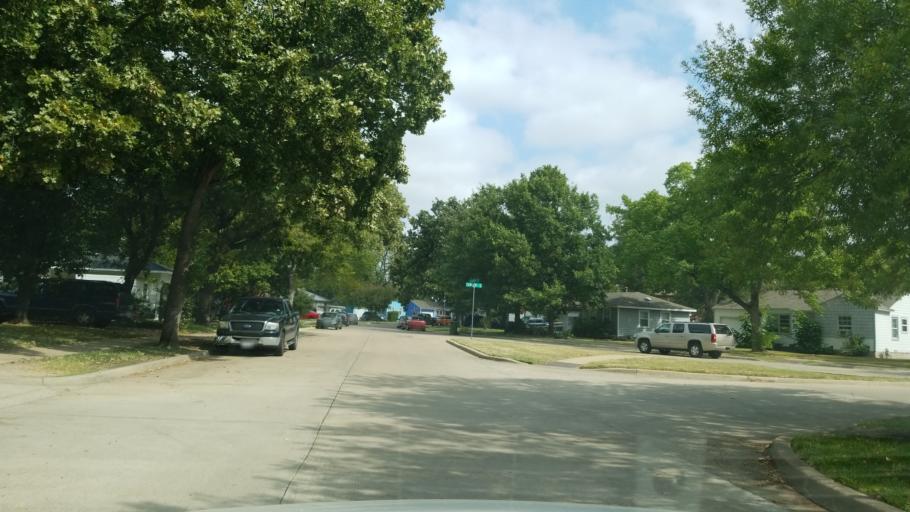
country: US
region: Texas
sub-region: Dallas County
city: Garland
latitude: 32.8920
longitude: -96.6496
